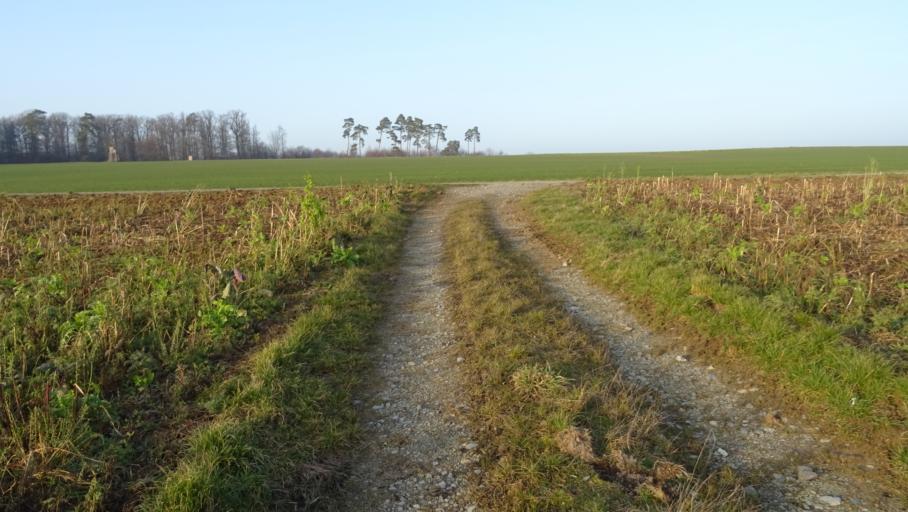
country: DE
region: Baden-Wuerttemberg
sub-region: Karlsruhe Region
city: Neckargerach
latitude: 49.4032
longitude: 9.1132
